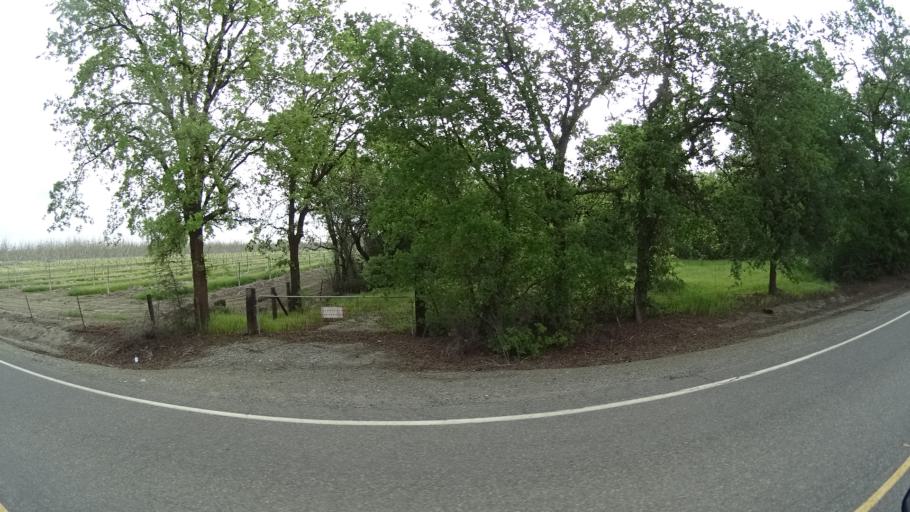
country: US
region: California
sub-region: Colusa County
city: Colusa
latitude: 39.4213
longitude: -121.9667
